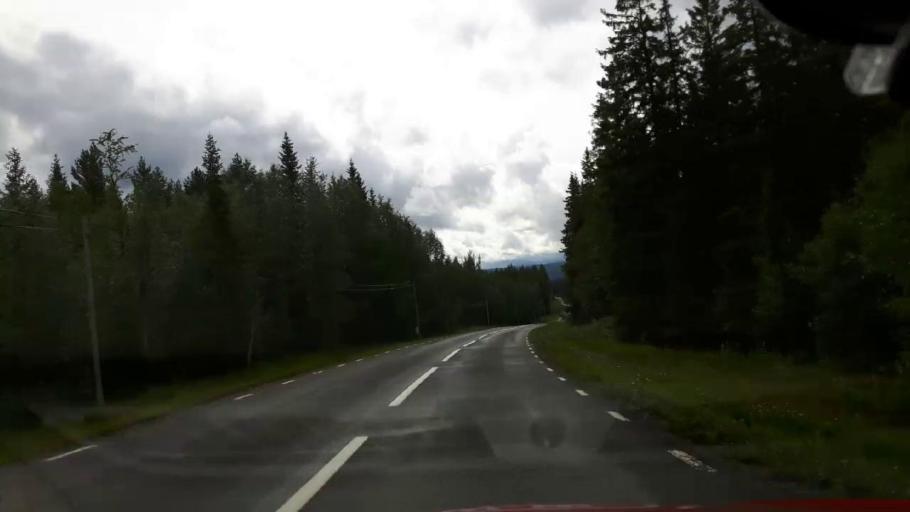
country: NO
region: Nord-Trondelag
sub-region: Lierne
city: Sandvika
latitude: 64.5183
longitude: 14.1618
